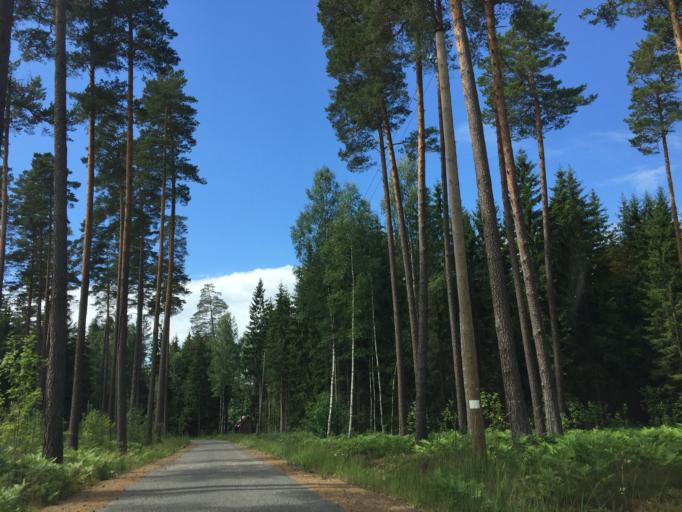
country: LV
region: Saulkrastu
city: Saulkrasti
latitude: 57.3506
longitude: 24.4327
